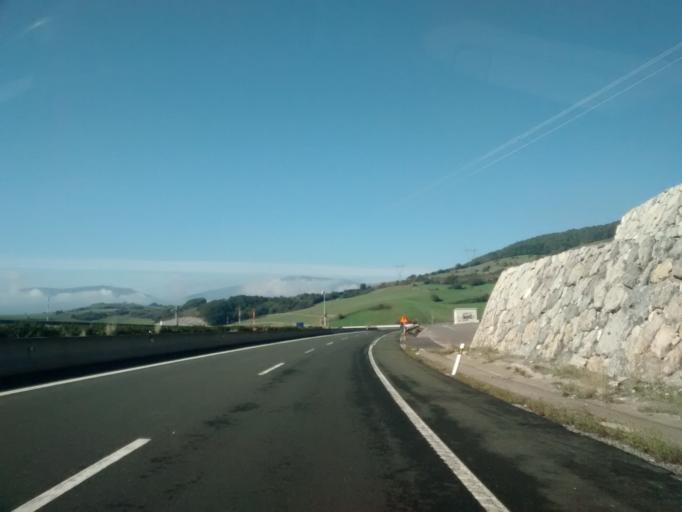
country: ES
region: Cantabria
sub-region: Provincia de Cantabria
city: Reinosa
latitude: 43.0223
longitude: -4.1175
